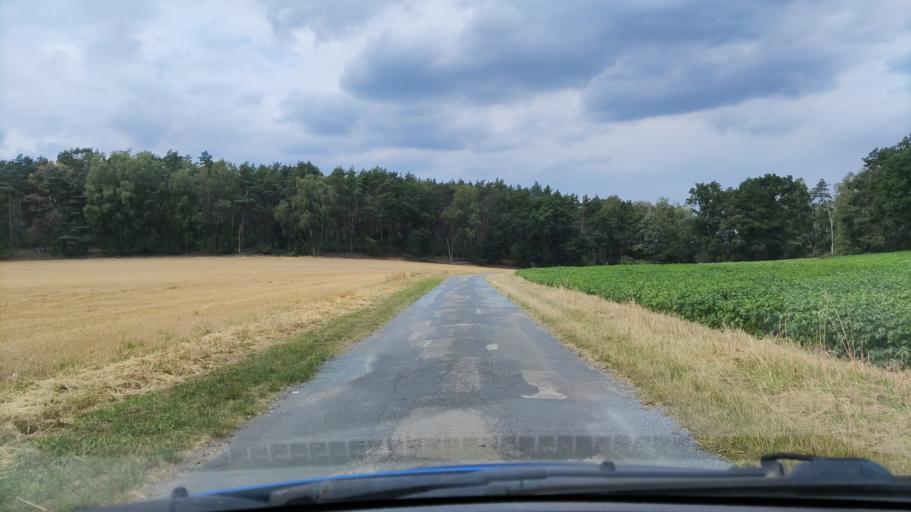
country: DE
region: Lower Saxony
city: Schnega
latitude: 52.9433
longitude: 10.8731
